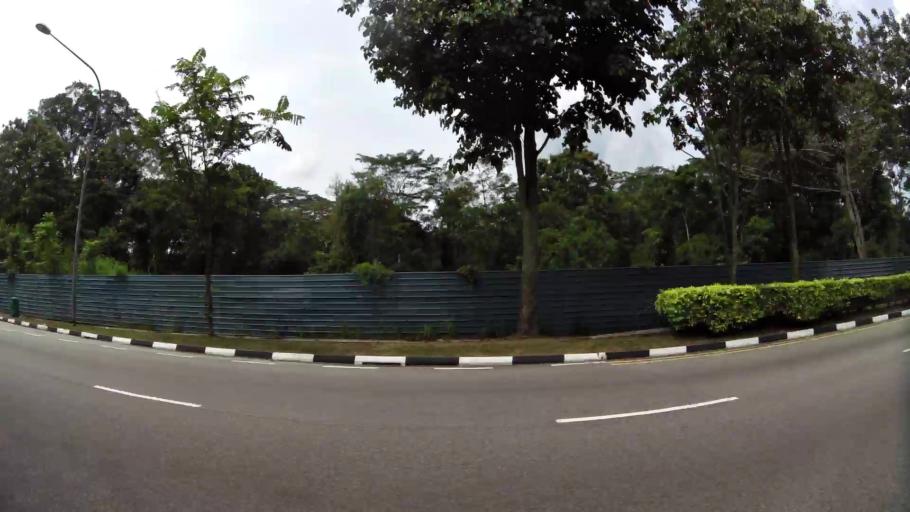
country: MY
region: Johor
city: Johor Bahru
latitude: 1.3561
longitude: 103.7367
